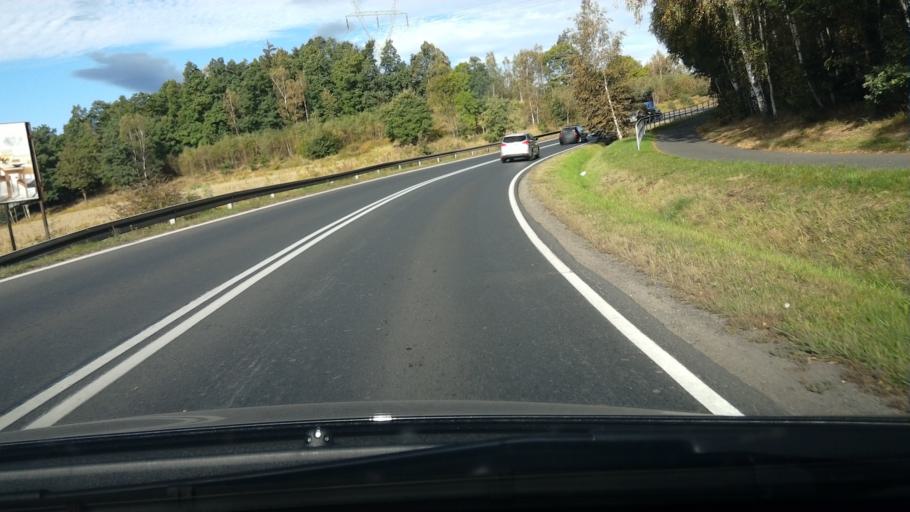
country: PL
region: Lower Silesian Voivodeship
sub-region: Powiat jeleniogorski
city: Myslakowice
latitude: 50.8666
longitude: 15.7685
